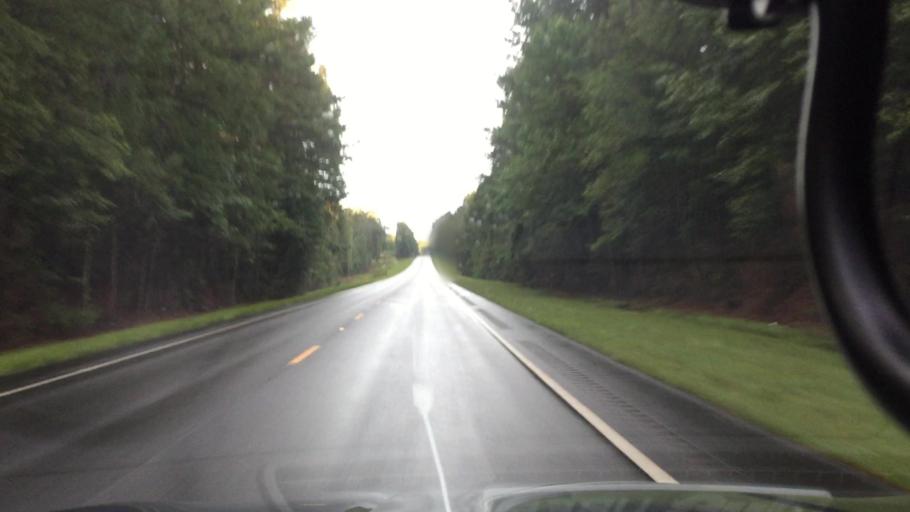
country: US
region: Alabama
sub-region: Coffee County
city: New Brockton
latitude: 31.5655
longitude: -85.9258
